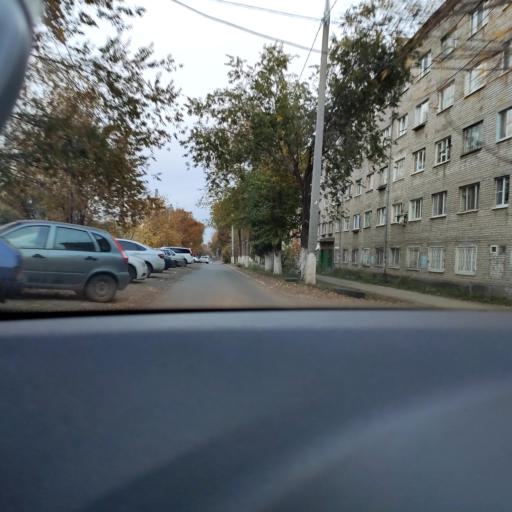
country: RU
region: Samara
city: Samara
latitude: 53.2181
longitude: 50.2317
